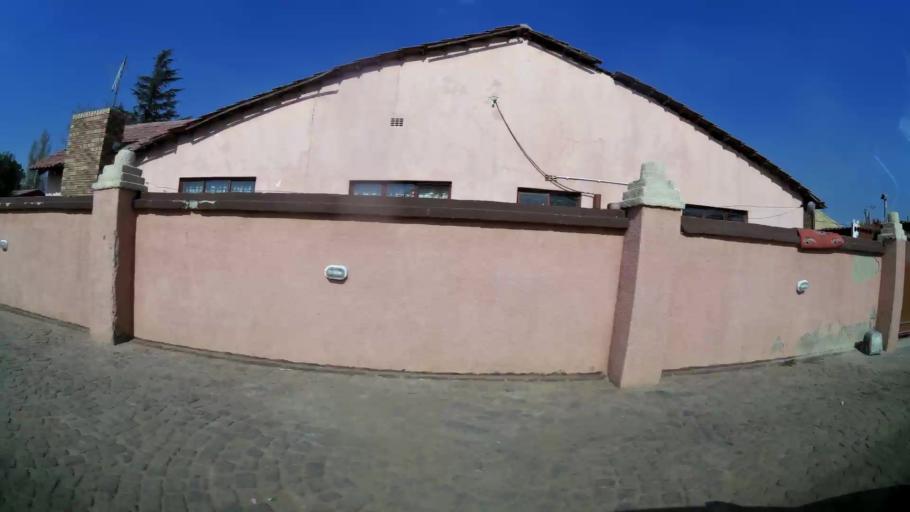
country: ZA
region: Gauteng
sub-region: Ekurhuleni Metropolitan Municipality
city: Brakpan
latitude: -26.1374
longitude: 28.4283
